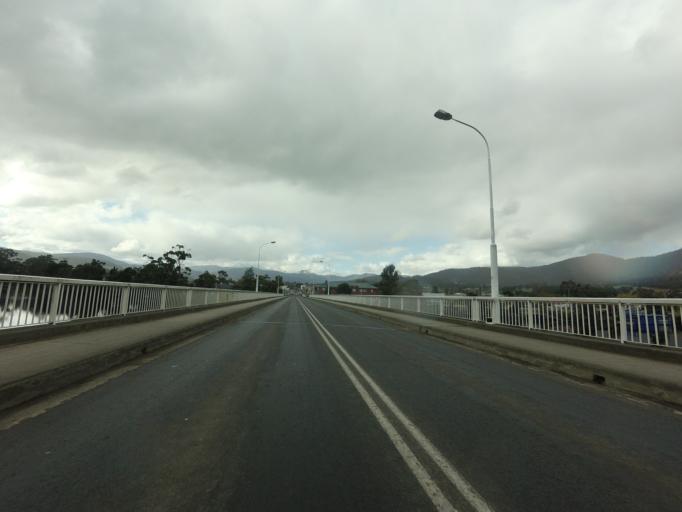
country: AU
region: Tasmania
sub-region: Huon Valley
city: Huonville
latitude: -43.0342
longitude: 147.0463
